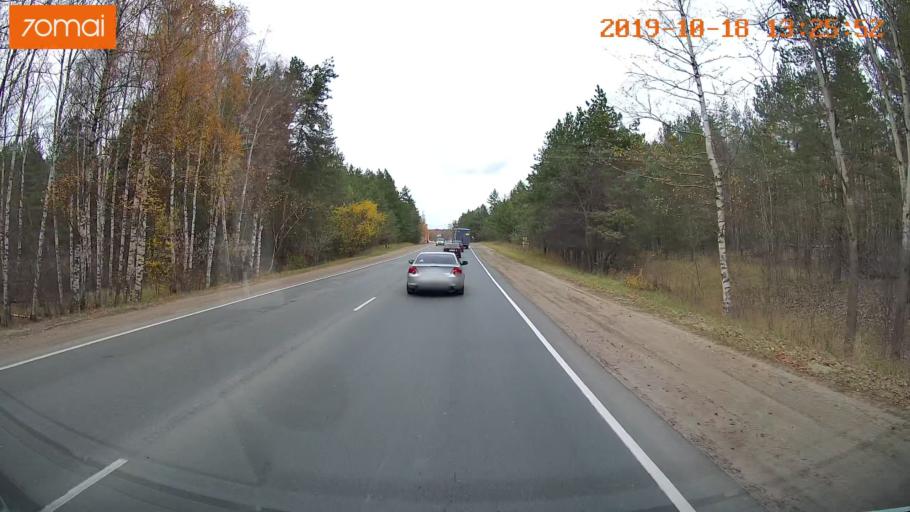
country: RU
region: Rjazan
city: Polyany
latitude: 54.7469
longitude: 39.8400
